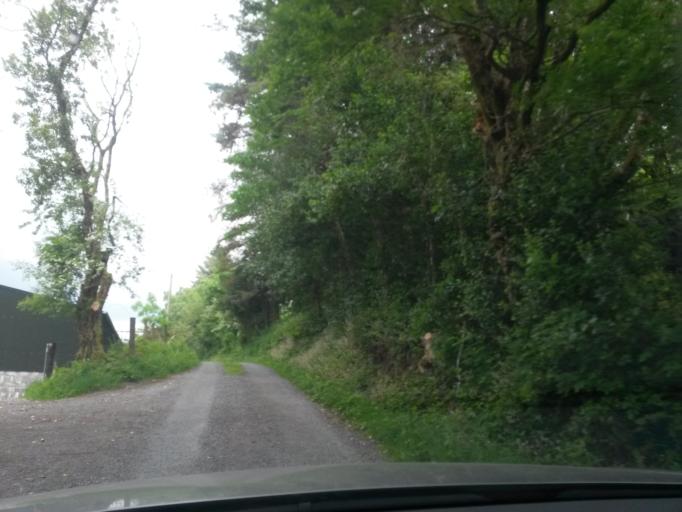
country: IE
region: Munster
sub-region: Ciarrai
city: Kenmare
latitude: 51.8128
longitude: -9.5298
